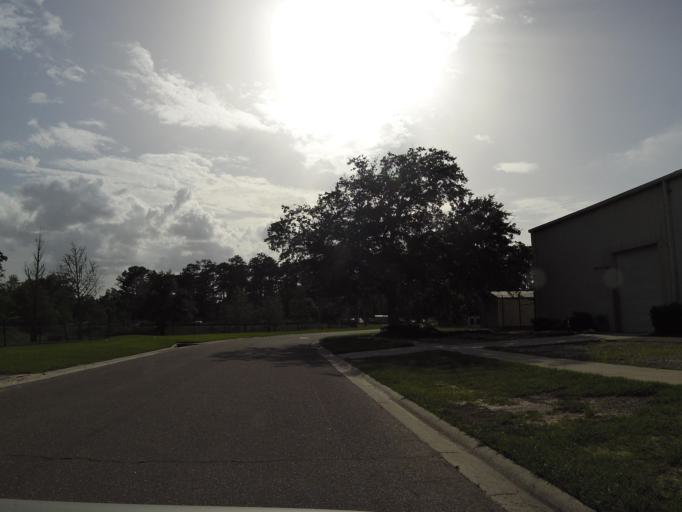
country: US
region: Florida
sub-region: Duval County
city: Jacksonville
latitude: 30.2886
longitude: -81.7352
